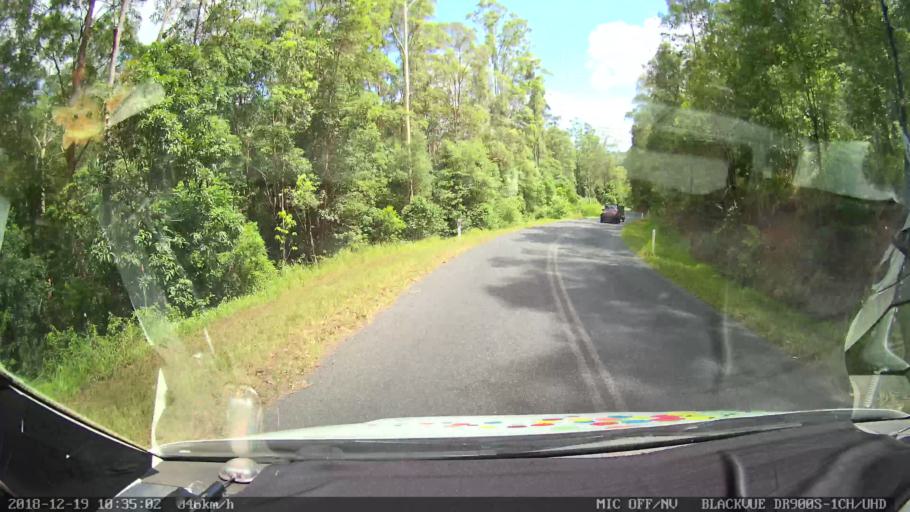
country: AU
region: New South Wales
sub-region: Lismore Municipality
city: Larnook
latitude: -28.5791
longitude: 153.1345
